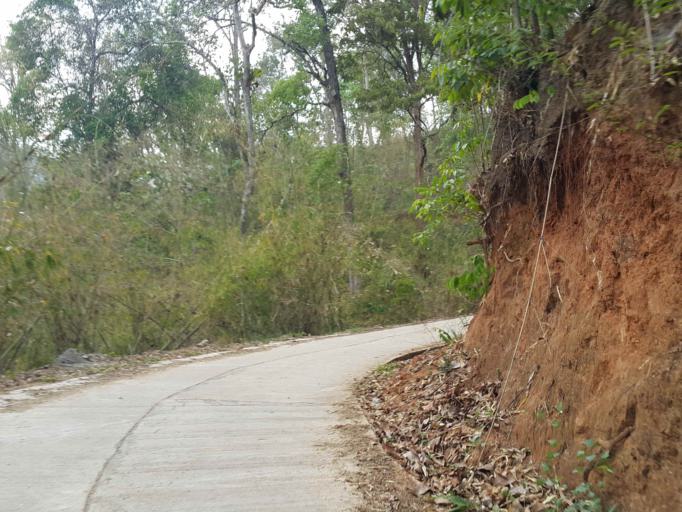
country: TH
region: Chiang Mai
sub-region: Amphoe Chiang Dao
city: Chiang Dao
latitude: 19.2834
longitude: 98.7607
